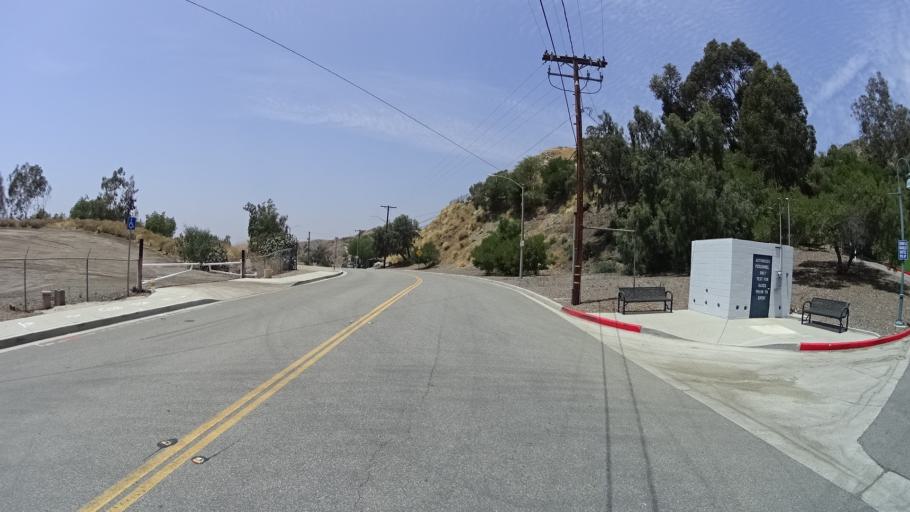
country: US
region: California
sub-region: Los Angeles County
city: Burbank
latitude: 34.2054
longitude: -118.3100
